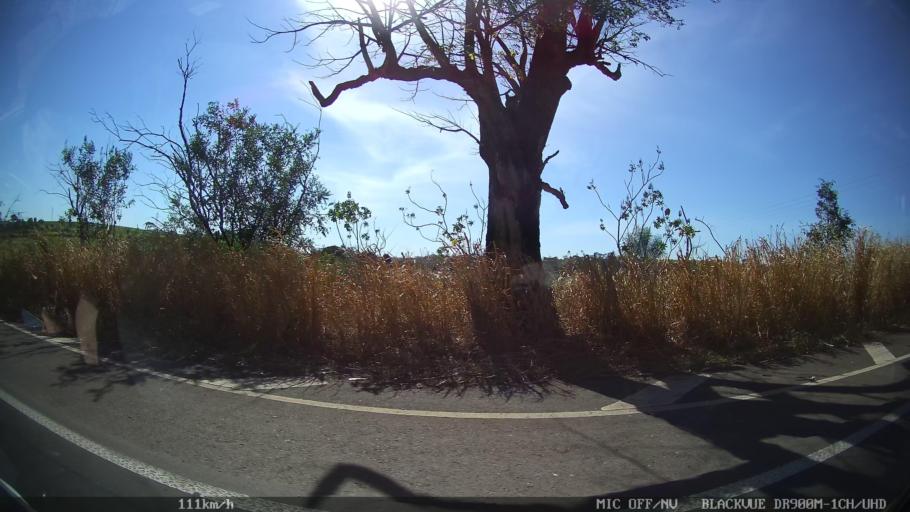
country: BR
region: Sao Paulo
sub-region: Olimpia
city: Olimpia
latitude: -20.6309
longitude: -48.8093
